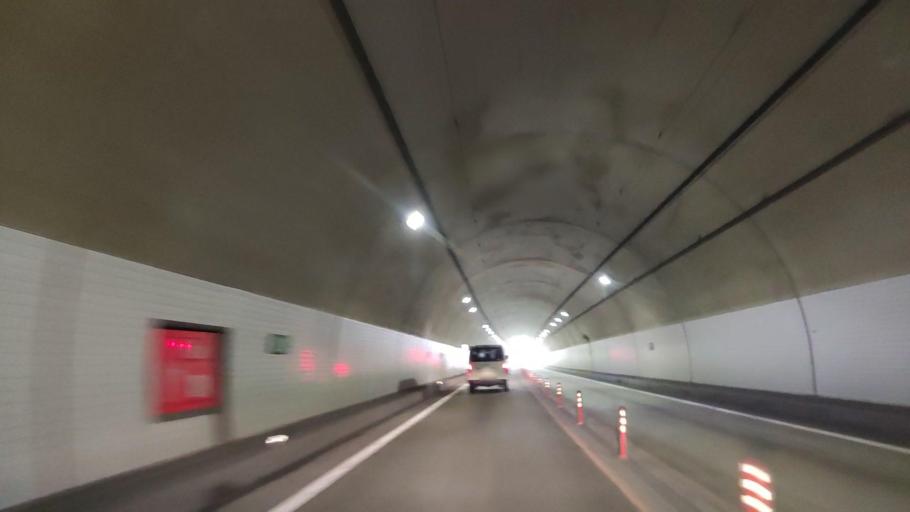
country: JP
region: Akita
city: Odate
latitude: 40.3462
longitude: 140.6657
